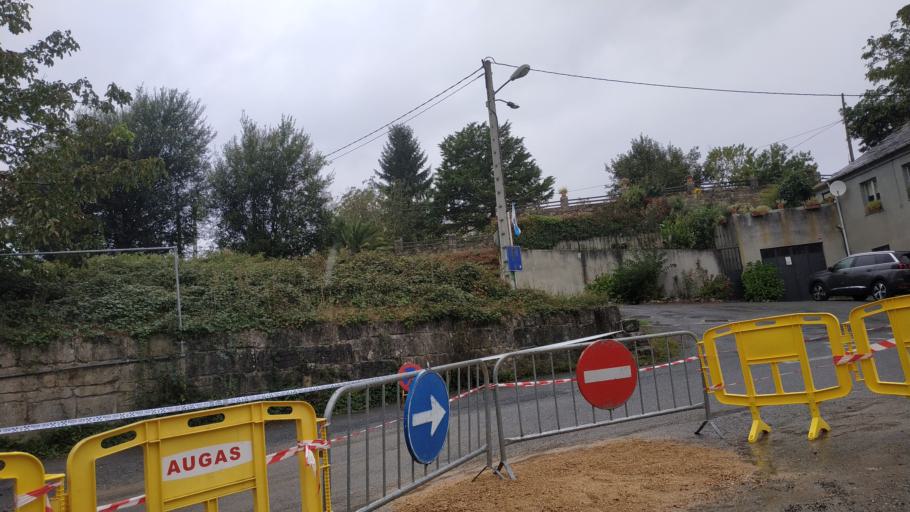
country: ES
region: Galicia
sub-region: Provincia de Lugo
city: Lugo
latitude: 43.0001
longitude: -7.5729
